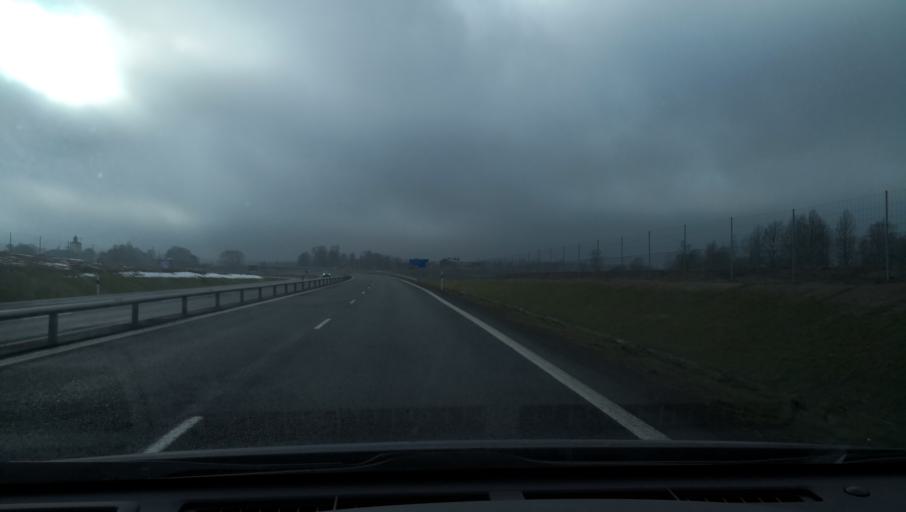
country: SE
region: Vaestra Goetaland
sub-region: Gullspangs Kommun
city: Hova
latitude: 58.8654
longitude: 14.2262
